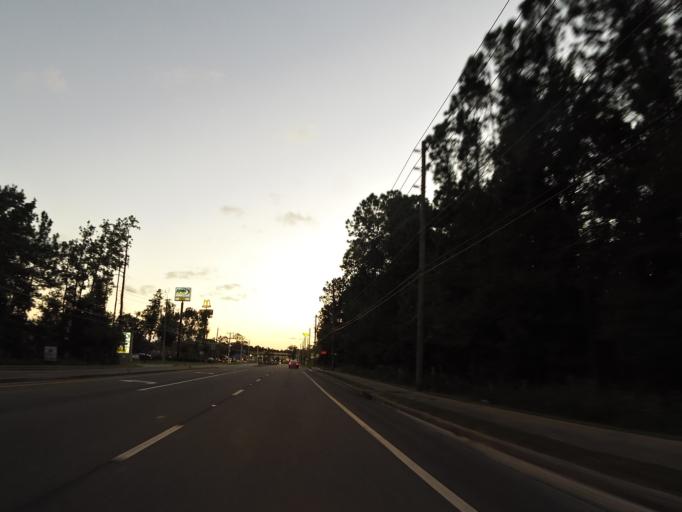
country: US
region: Florida
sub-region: Saint Johns County
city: Palm Valley
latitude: 30.0683
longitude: -81.4932
